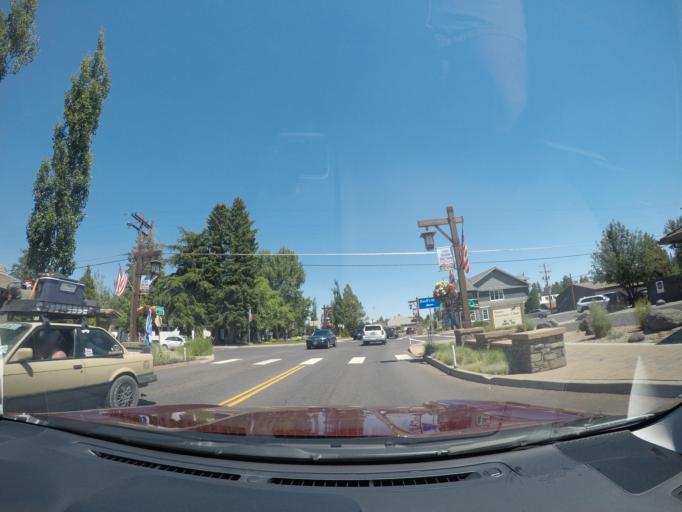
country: US
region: Oregon
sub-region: Deschutes County
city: Sisters
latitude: 44.2913
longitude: -121.5468
